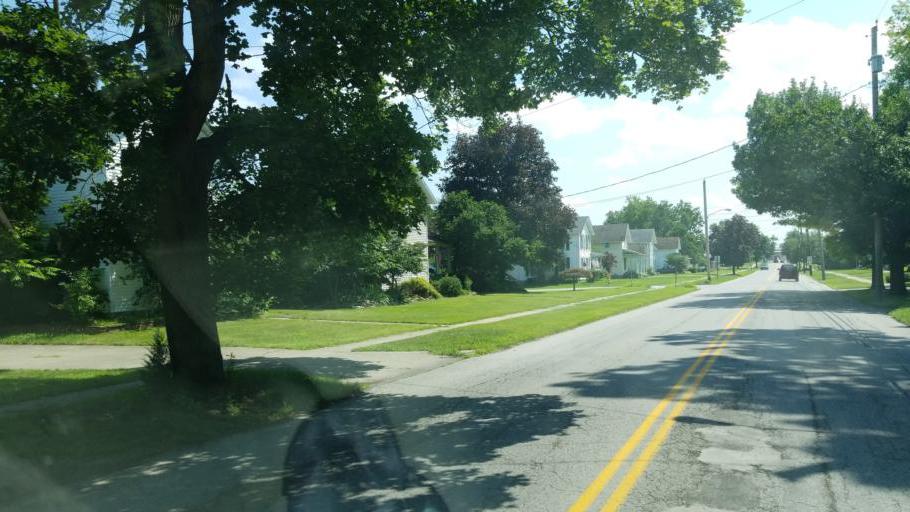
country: US
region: Ohio
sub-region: Huron County
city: Bellevue
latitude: 41.2805
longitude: -82.8390
